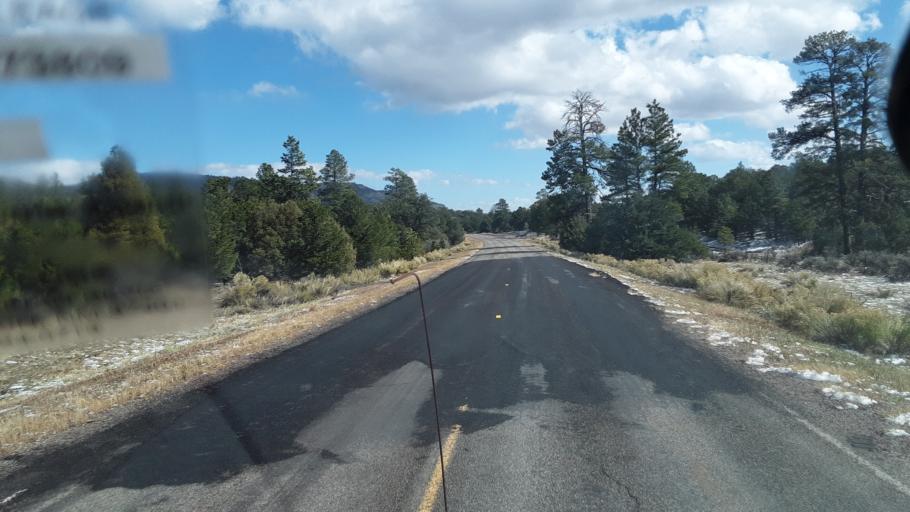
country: US
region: New Mexico
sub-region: Rio Arriba County
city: Santa Teresa
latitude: 36.2011
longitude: -106.7319
